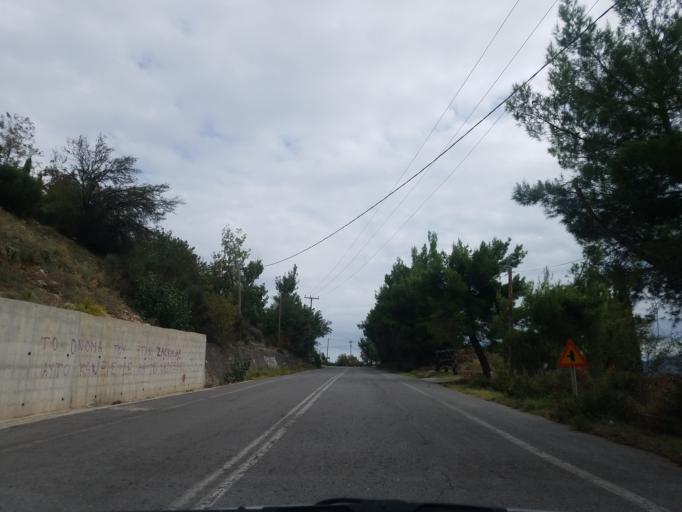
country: GR
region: Central Greece
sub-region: Nomos Voiotias
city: Arachova
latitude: 38.4844
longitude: 22.5714
